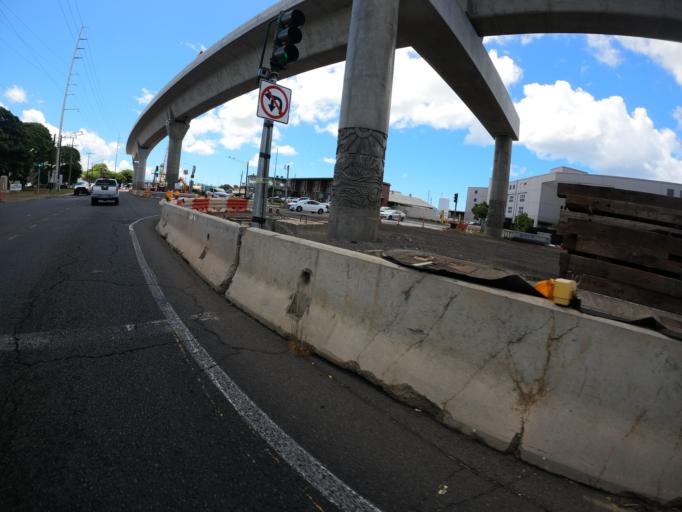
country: US
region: Hawaii
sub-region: Honolulu County
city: Honolulu
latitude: 21.3327
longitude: -157.8875
